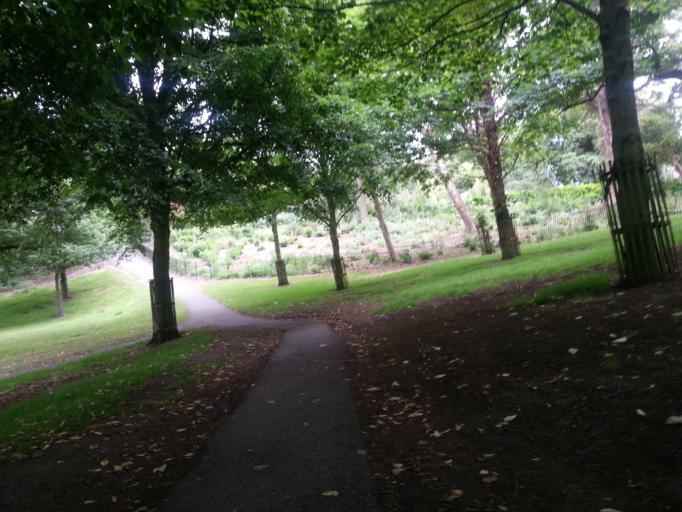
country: IE
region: Leinster
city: Rialto
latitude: 53.3517
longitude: -6.3038
